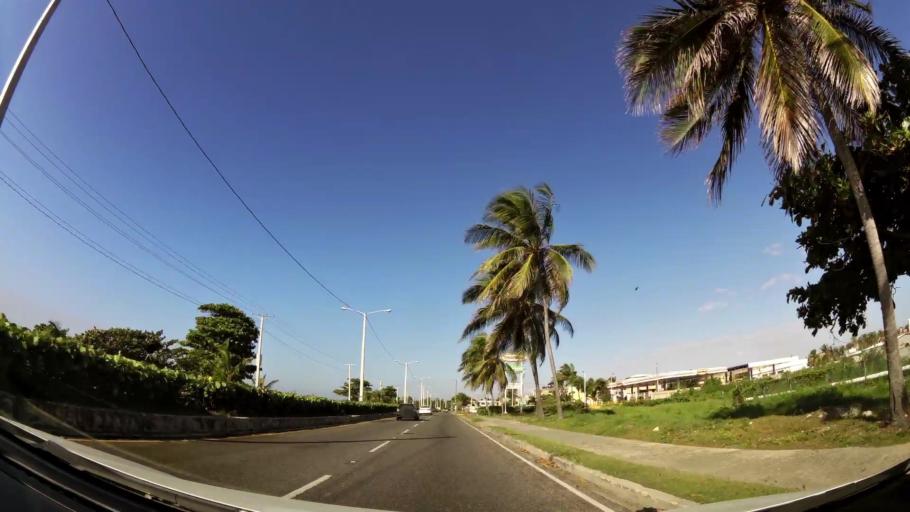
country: DO
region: Santo Domingo
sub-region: Santo Domingo
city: Santo Domingo Este
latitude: 18.4679
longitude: -69.8679
